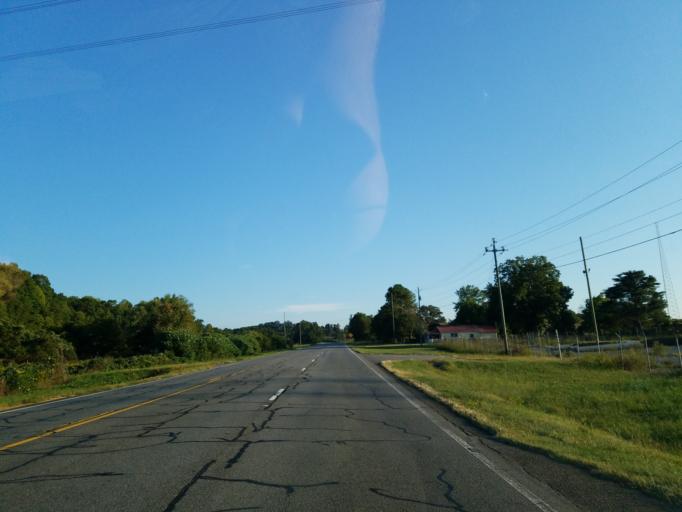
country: US
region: Georgia
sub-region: Bartow County
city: Rydal
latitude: 34.3926
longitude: -84.7069
